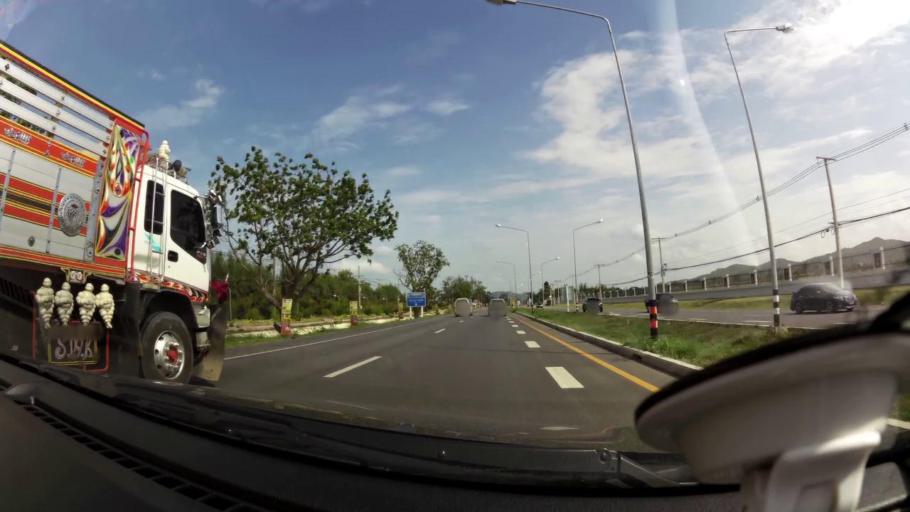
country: TH
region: Prachuap Khiri Khan
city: Hua Hin
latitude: 12.5028
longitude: 99.9683
